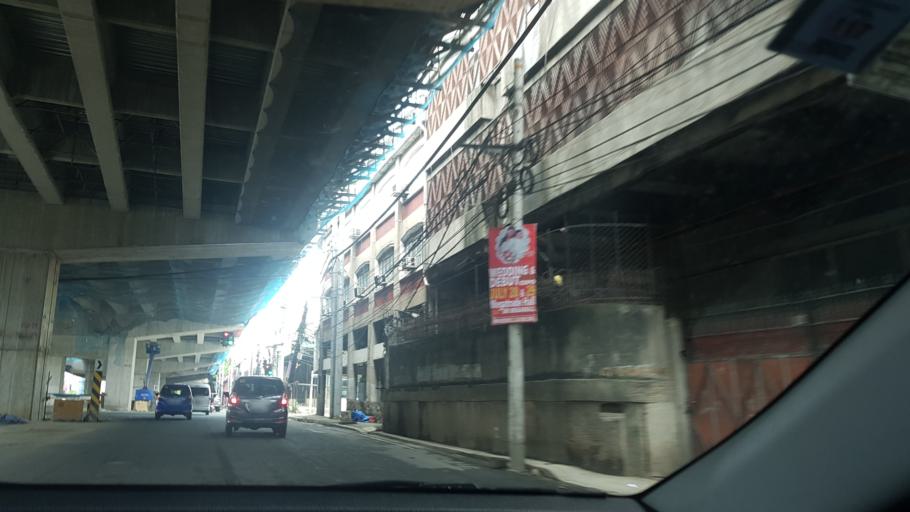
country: PH
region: Calabarzon
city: Del Monte
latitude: 14.6364
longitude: 121.0087
